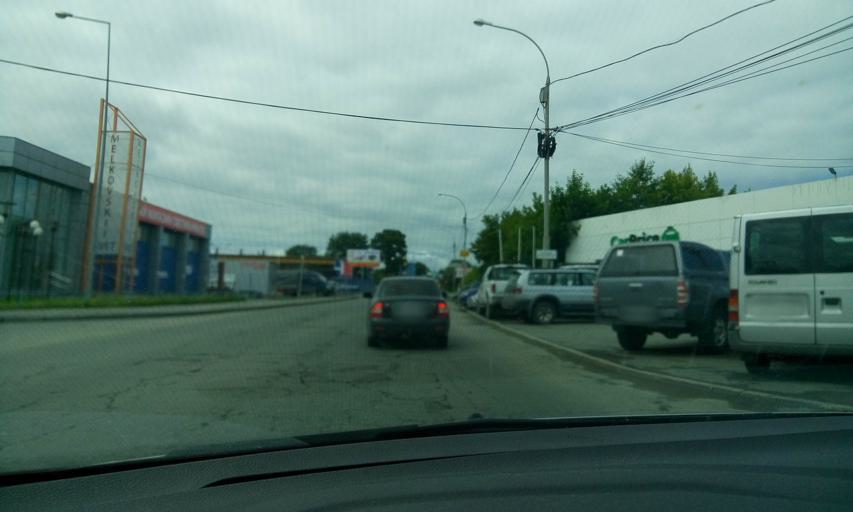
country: RU
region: Sverdlovsk
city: Yekaterinburg
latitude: 56.8626
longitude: 60.6074
